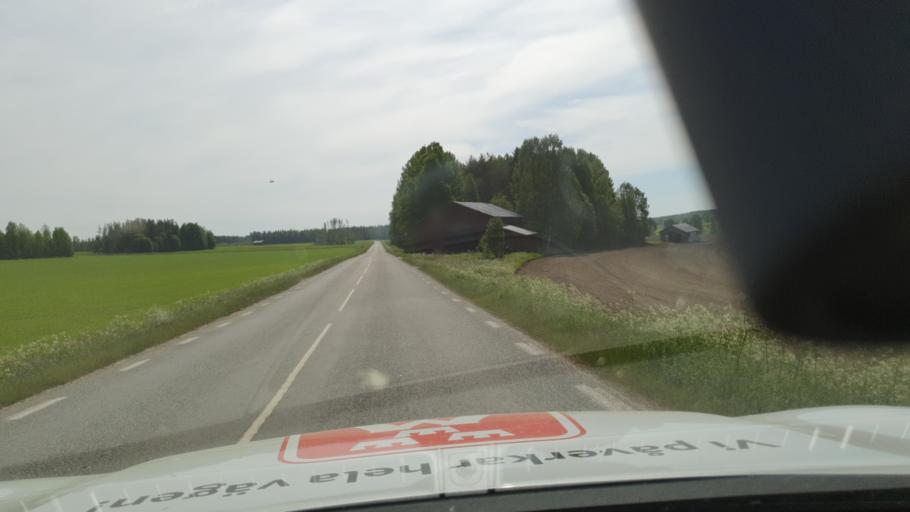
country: SE
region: Vaesterbotten
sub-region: Robertsfors Kommun
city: Robertsfors
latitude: 64.2985
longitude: 20.8820
